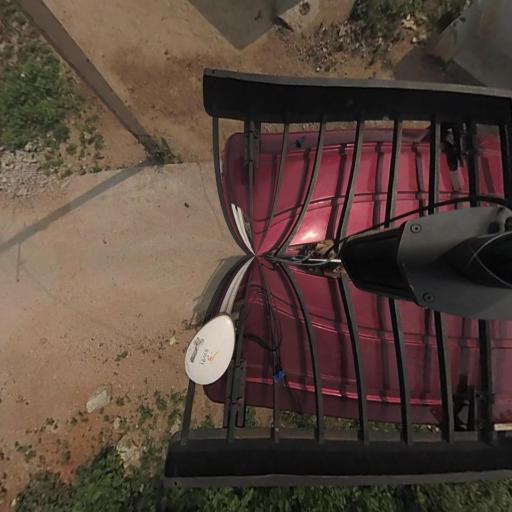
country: IN
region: Telangana
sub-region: Nalgonda
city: Nalgonda
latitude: 17.2081
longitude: 79.1578
